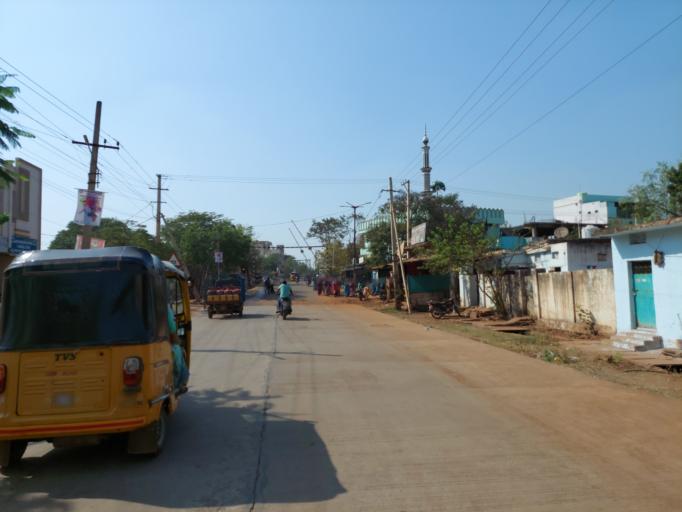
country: IN
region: Telangana
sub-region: Rangareddi
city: Vikarabad
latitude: 17.3382
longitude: 77.8995
